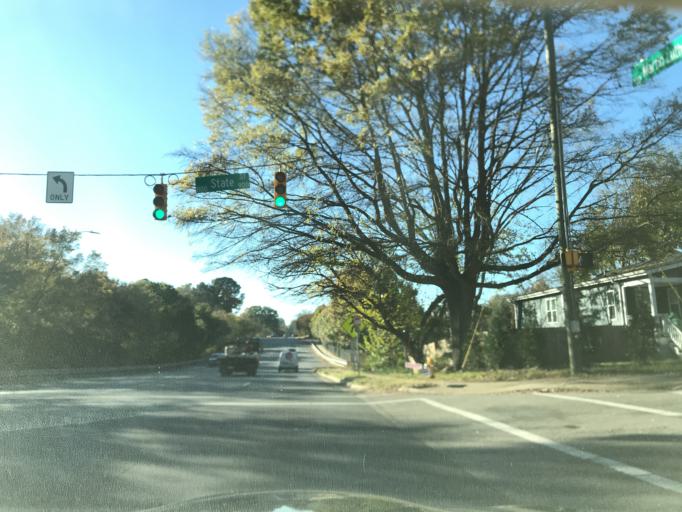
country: US
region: North Carolina
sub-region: Wake County
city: Raleigh
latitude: 35.7679
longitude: -78.6244
